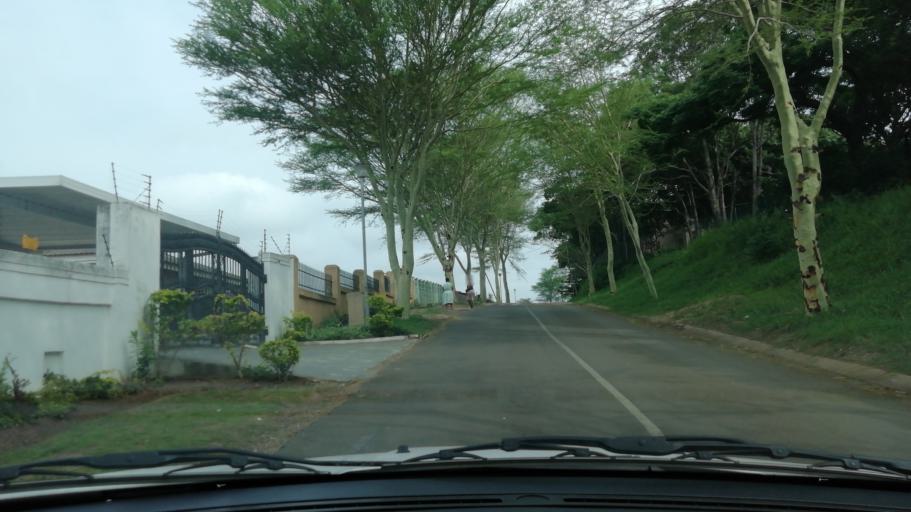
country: ZA
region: KwaZulu-Natal
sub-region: uThungulu District Municipality
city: Empangeni
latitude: -28.7396
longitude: 31.8790
